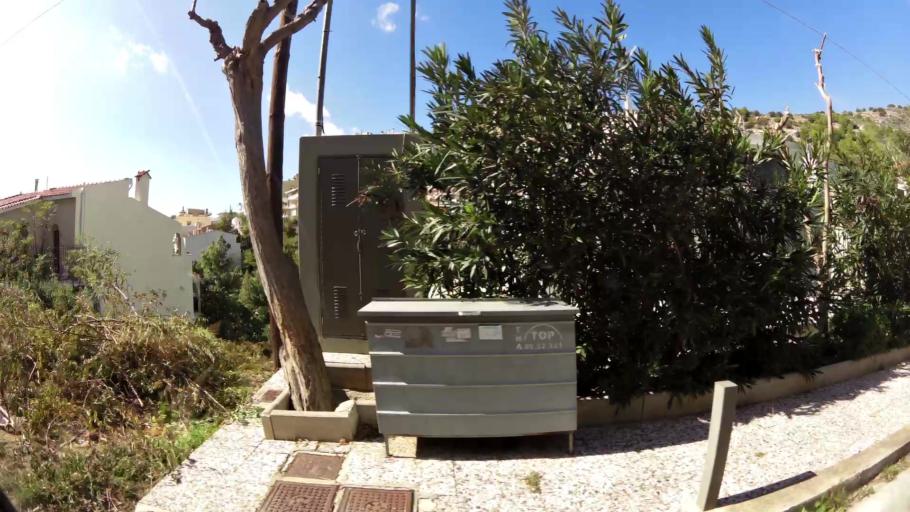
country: GR
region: Attica
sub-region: Nomarchia Anatolikis Attikis
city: Voula
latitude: 37.8607
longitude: 23.7817
